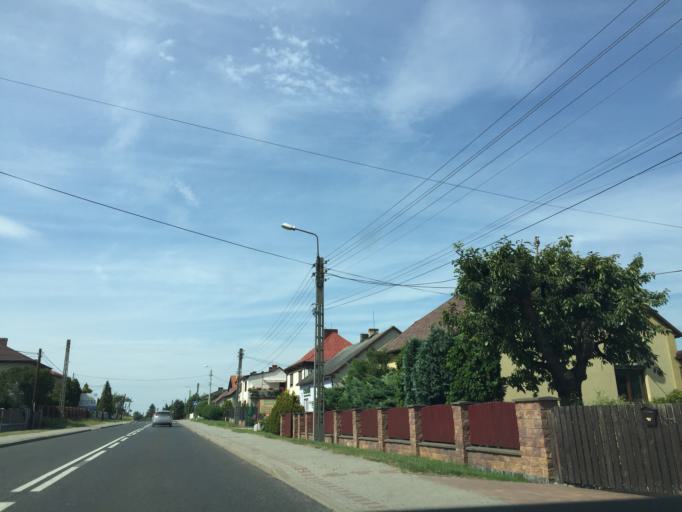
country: PL
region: Silesian Voivodeship
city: Gorzyczki
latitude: 49.9502
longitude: 18.4035
